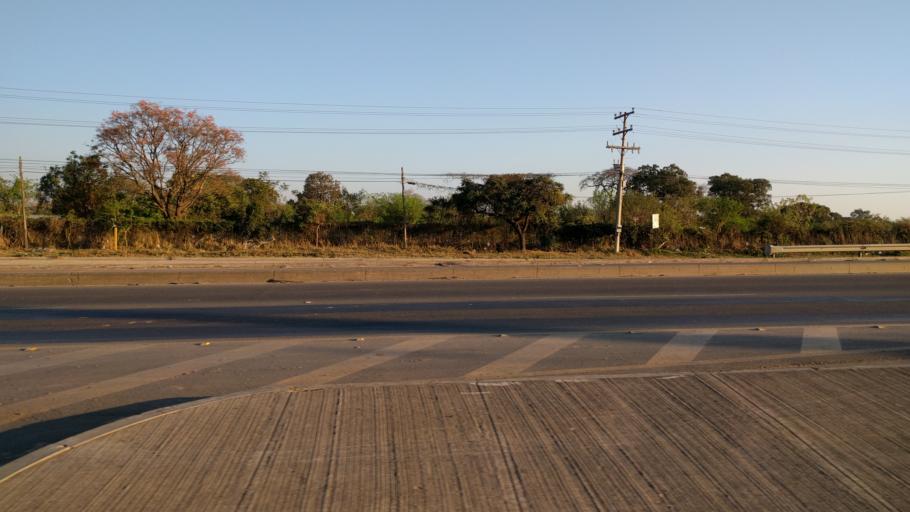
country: BO
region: Santa Cruz
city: Cotoca
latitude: -17.7648
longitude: -63.0785
